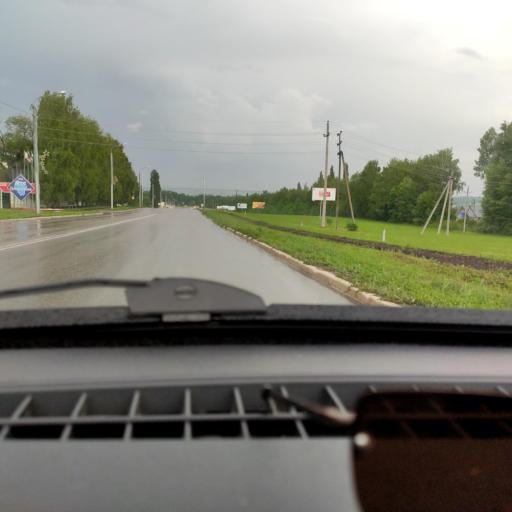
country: RU
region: Bashkortostan
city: Birsk
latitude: 55.4175
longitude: 55.5715
